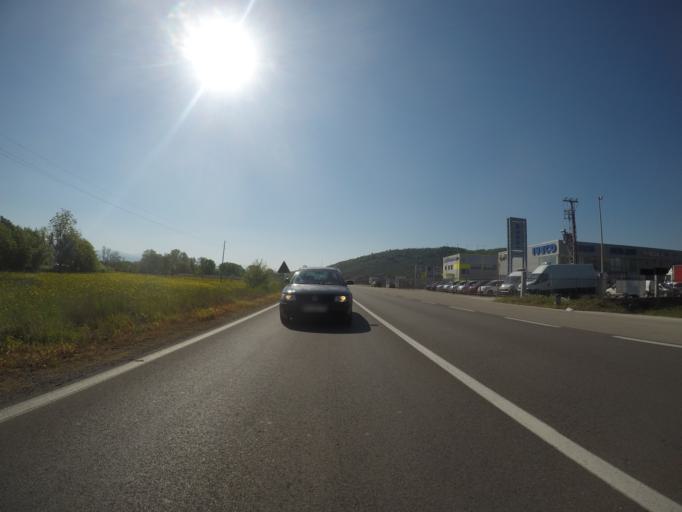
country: ME
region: Danilovgrad
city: Danilovgrad
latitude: 42.5131
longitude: 19.1270
